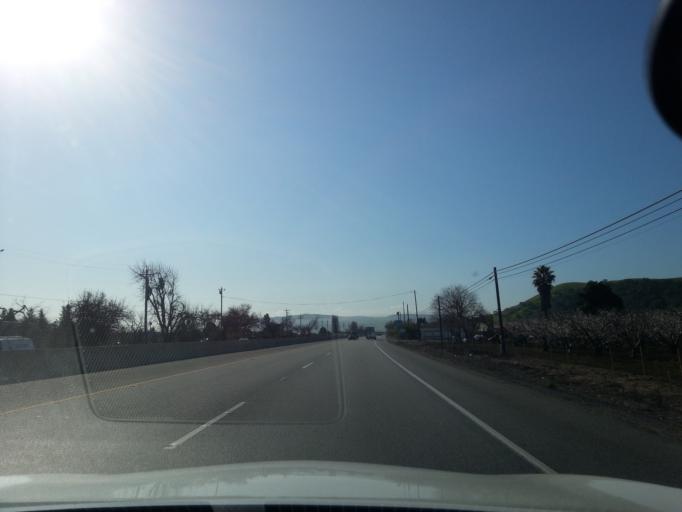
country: US
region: California
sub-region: Santa Clara County
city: Gilroy
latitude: 36.9746
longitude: -121.5551
